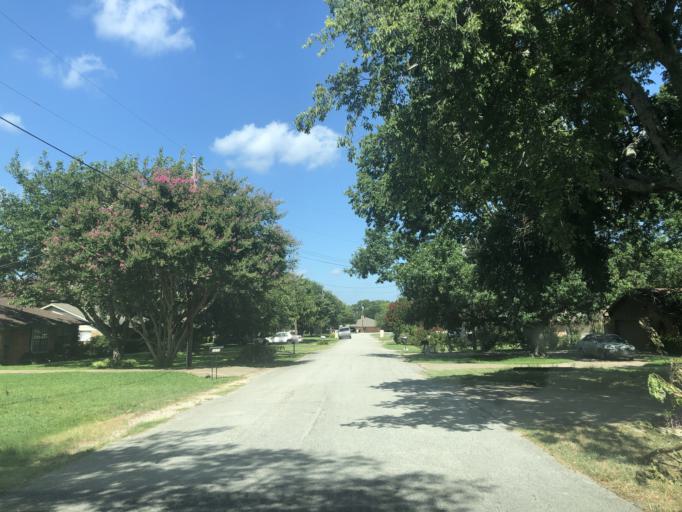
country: US
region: Texas
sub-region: Dallas County
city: Duncanville
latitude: 32.6482
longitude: -96.9359
